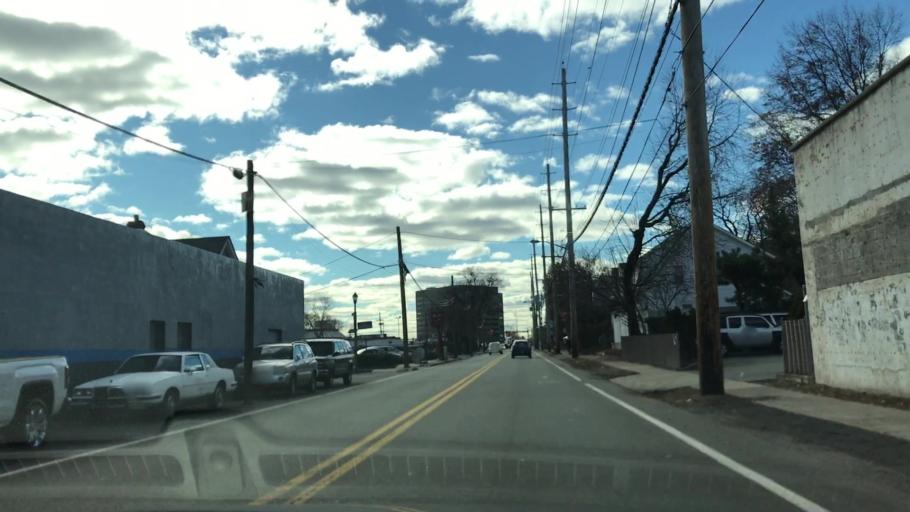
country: US
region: New Jersey
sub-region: Bergen County
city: Rutherford
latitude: 40.8240
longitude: -74.1001
